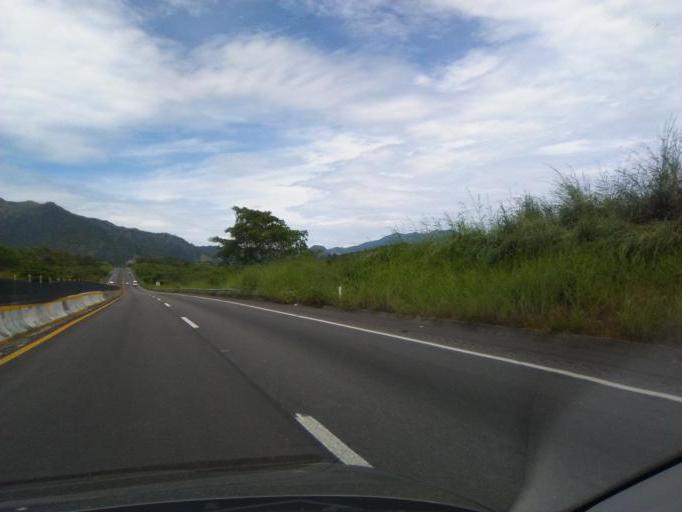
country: MX
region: Guerrero
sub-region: Chilpancingo de los Bravo
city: Cajelitos
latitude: 17.2683
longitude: -99.5119
